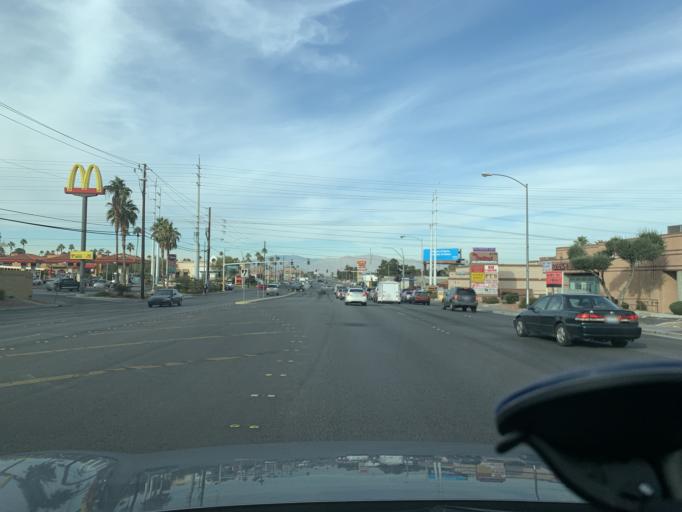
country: US
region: Nevada
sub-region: Clark County
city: Spring Valley
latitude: 36.1142
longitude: -115.2080
